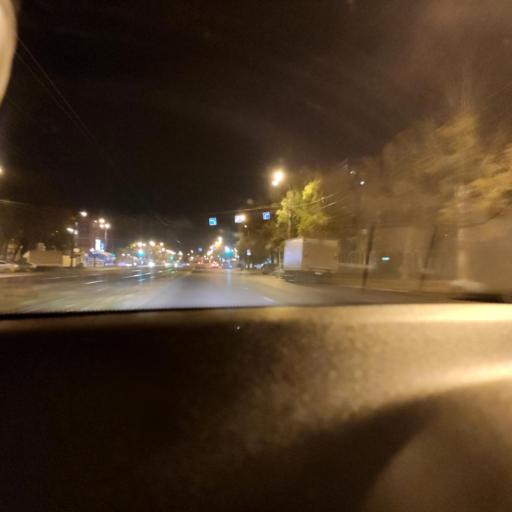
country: RU
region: Samara
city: Samara
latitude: 53.2081
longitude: 50.2332
